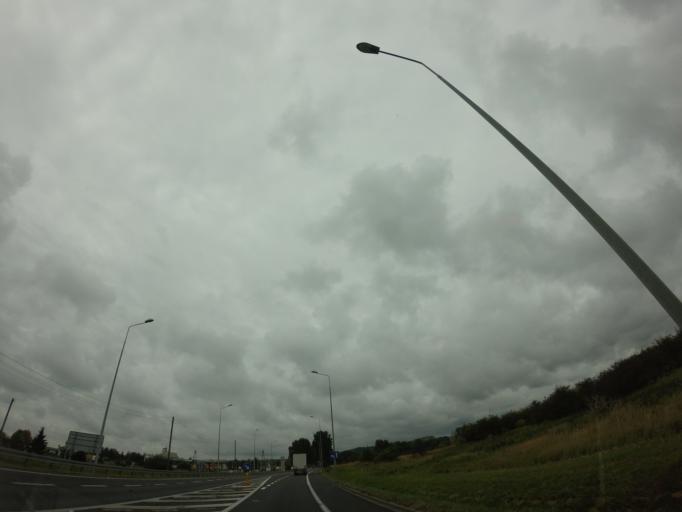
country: PL
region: West Pomeranian Voivodeship
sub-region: Powiat kamienski
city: Wolin
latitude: 53.8489
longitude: 14.6023
